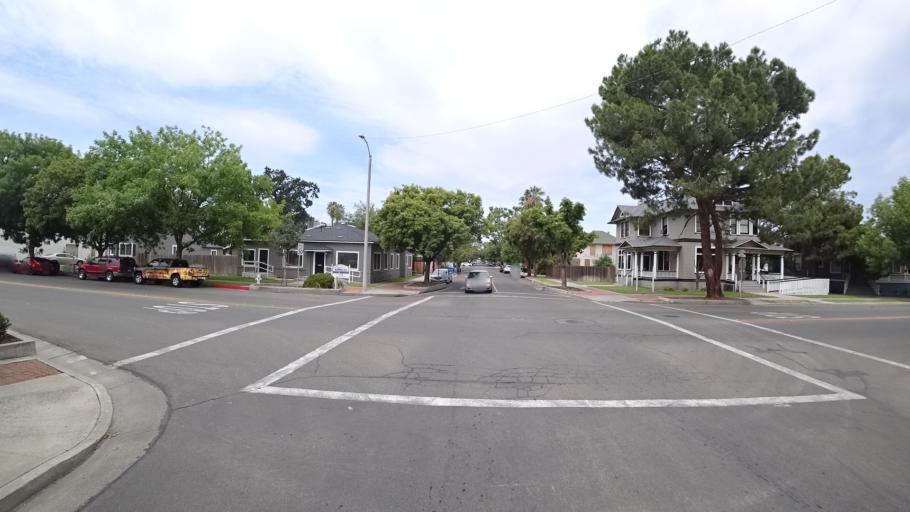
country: US
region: California
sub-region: Kings County
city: Hanford
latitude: 36.3322
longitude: -119.6476
